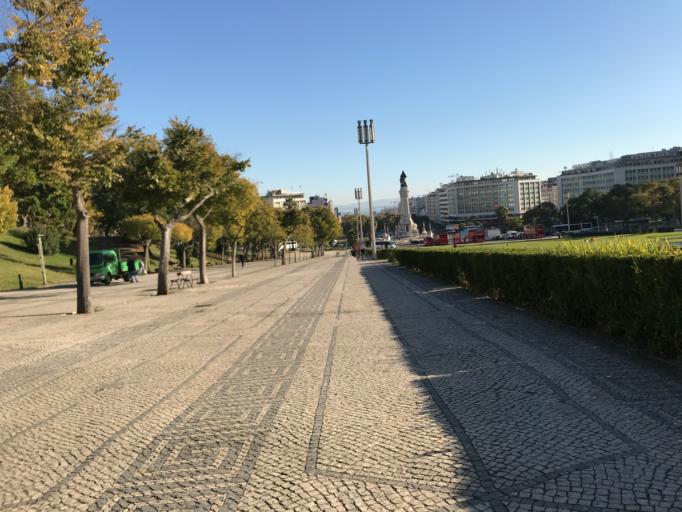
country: PT
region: Lisbon
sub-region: Lisbon
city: Lisbon
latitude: 38.7277
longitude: -9.1517
